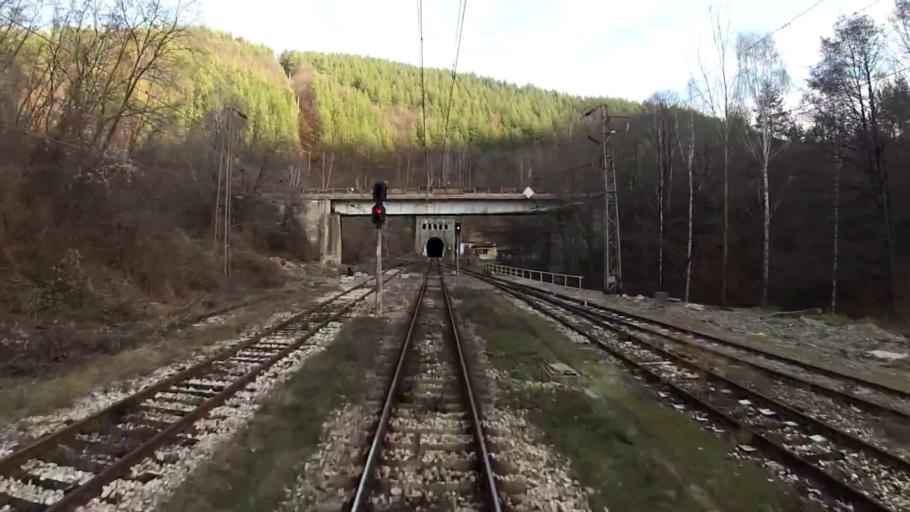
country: BG
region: Sofiya
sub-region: Obshtina Koprivshtitsa
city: Koprivshtitsa
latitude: 42.7002
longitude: 24.3502
